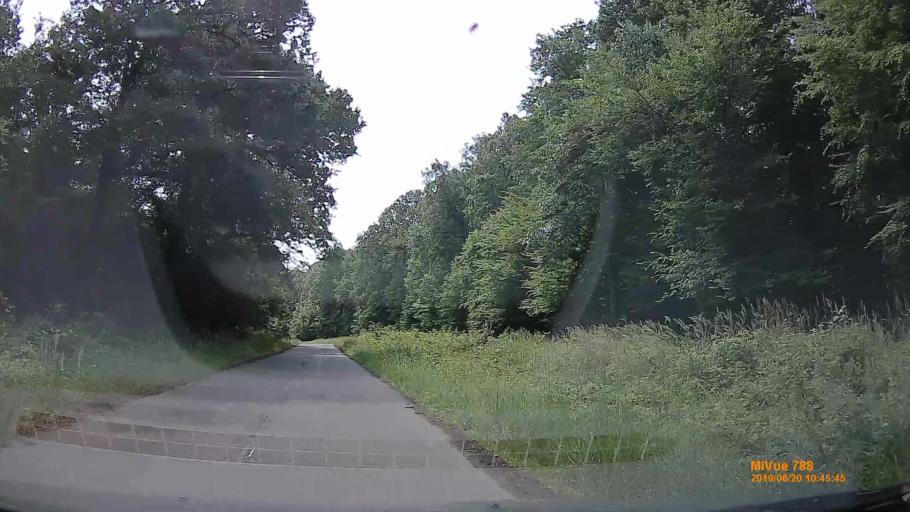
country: HU
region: Baranya
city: Hidas
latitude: 46.1815
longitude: 18.5731
